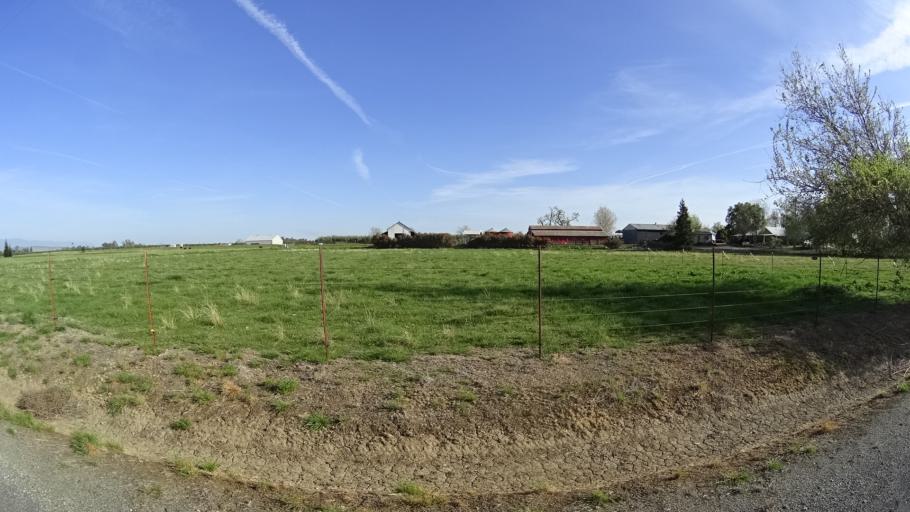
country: US
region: California
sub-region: Glenn County
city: Orland
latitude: 39.7188
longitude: -122.2364
